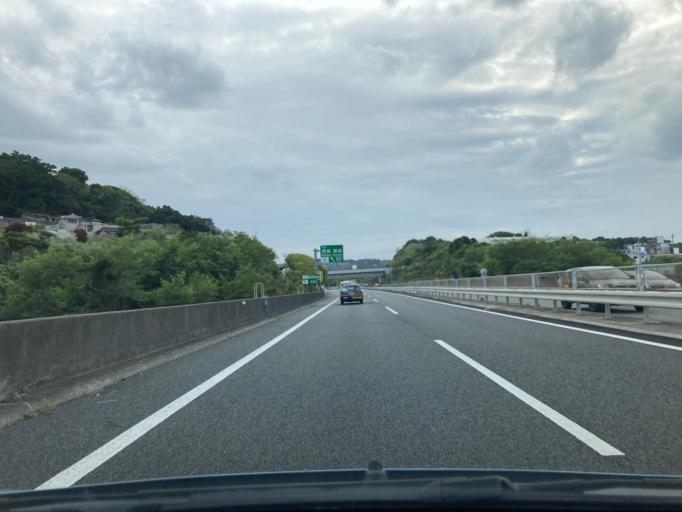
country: JP
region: Okinawa
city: Ginowan
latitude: 26.2487
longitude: 127.7548
